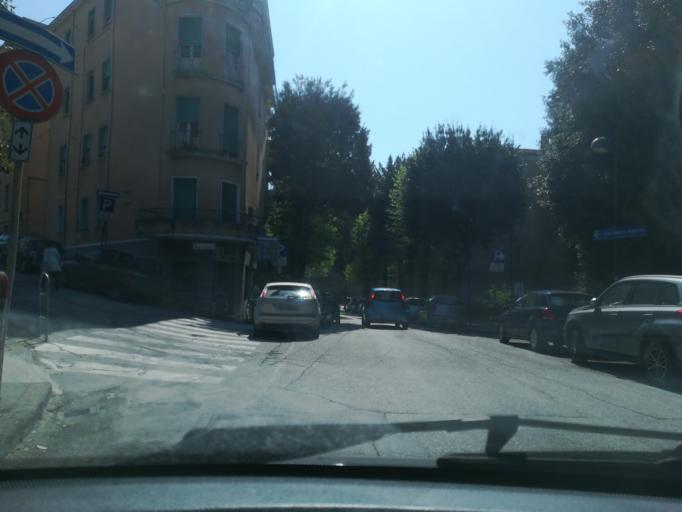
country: IT
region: The Marches
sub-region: Provincia di Macerata
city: Macerata
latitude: 43.2934
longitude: 13.4585
